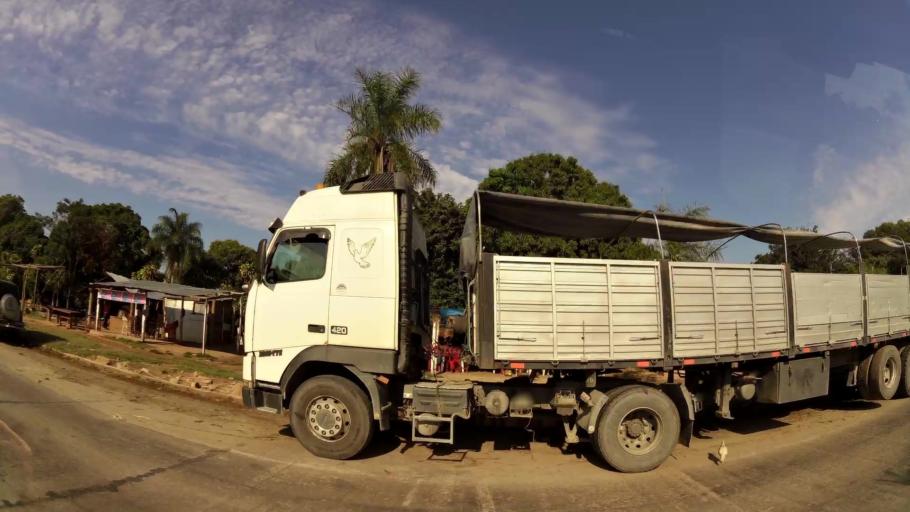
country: BO
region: Santa Cruz
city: Santa Cruz de la Sierra
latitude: -17.7081
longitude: -63.1268
